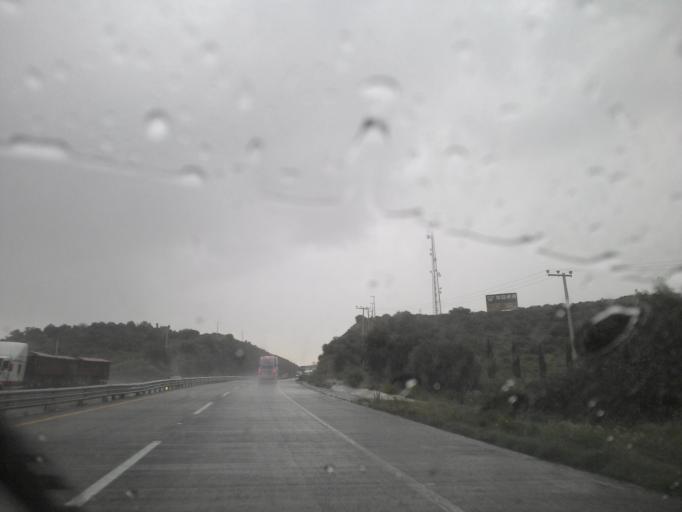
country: MX
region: Hidalgo
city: Zempoala
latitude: 19.8857
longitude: -98.6519
